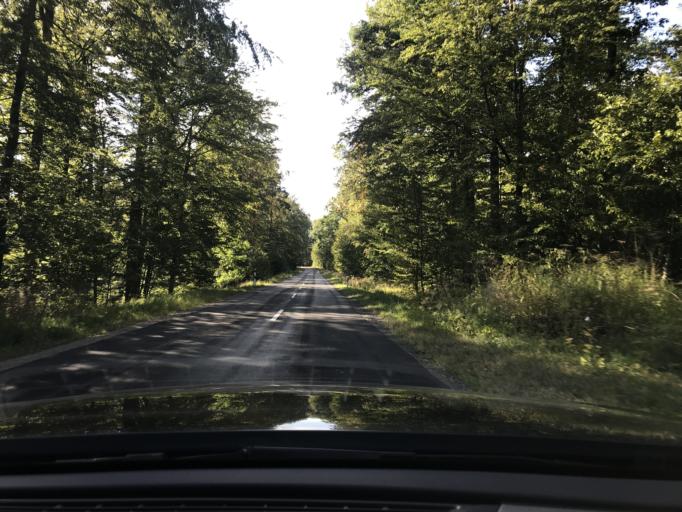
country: DE
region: Bavaria
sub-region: Regierungsbezirk Unterfranken
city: Burgpreppach
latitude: 50.0791
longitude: 10.6536
